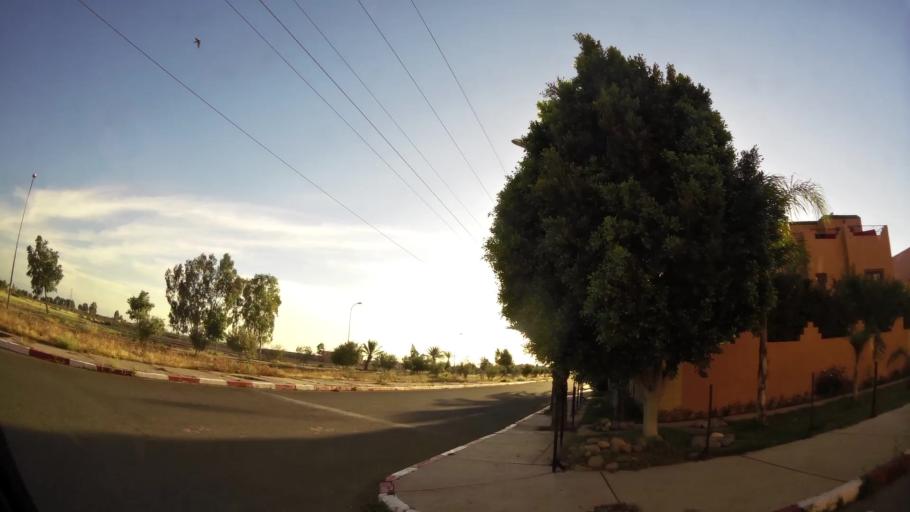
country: MA
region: Marrakech-Tensift-Al Haouz
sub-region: Marrakech
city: Marrakesh
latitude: 31.7429
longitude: -8.1117
